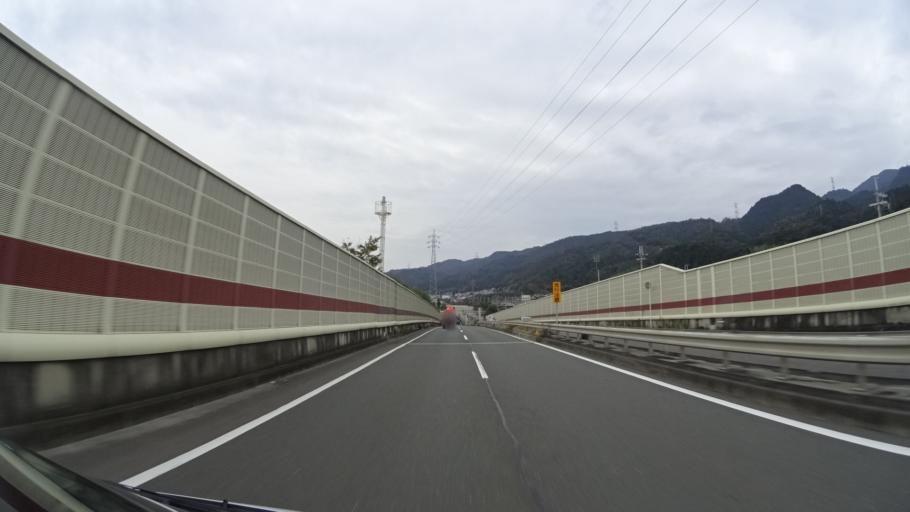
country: JP
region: Shiga Prefecture
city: Otsu-shi
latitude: 35.0523
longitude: 135.8656
